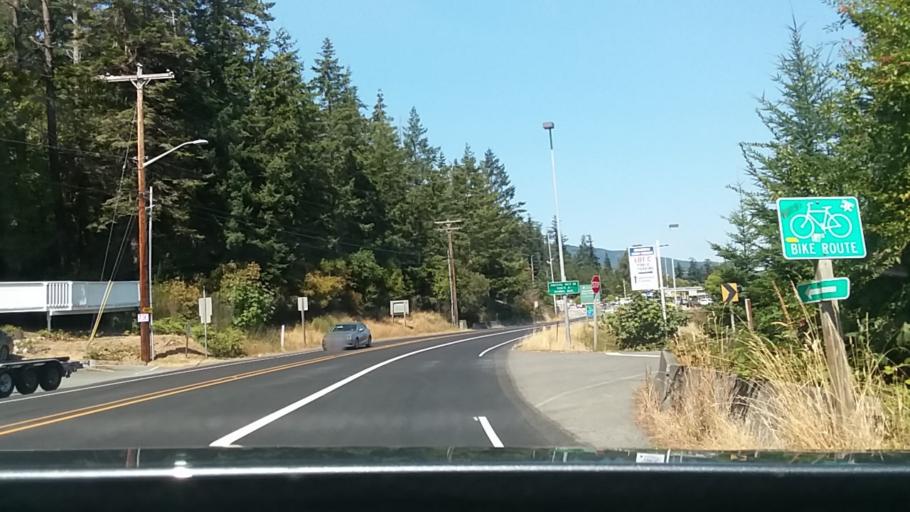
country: US
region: Washington
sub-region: Skagit County
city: Anacortes
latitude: 48.5013
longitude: -122.6791
